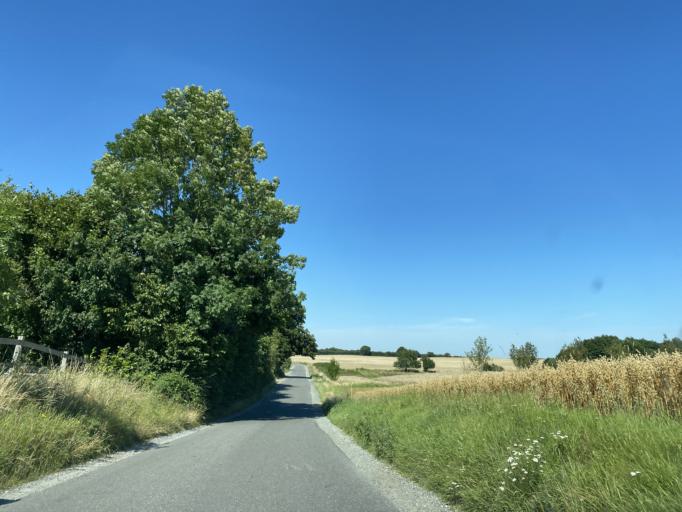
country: DK
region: South Denmark
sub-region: Kolding Kommune
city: Kolding
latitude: 55.5164
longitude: 9.5108
